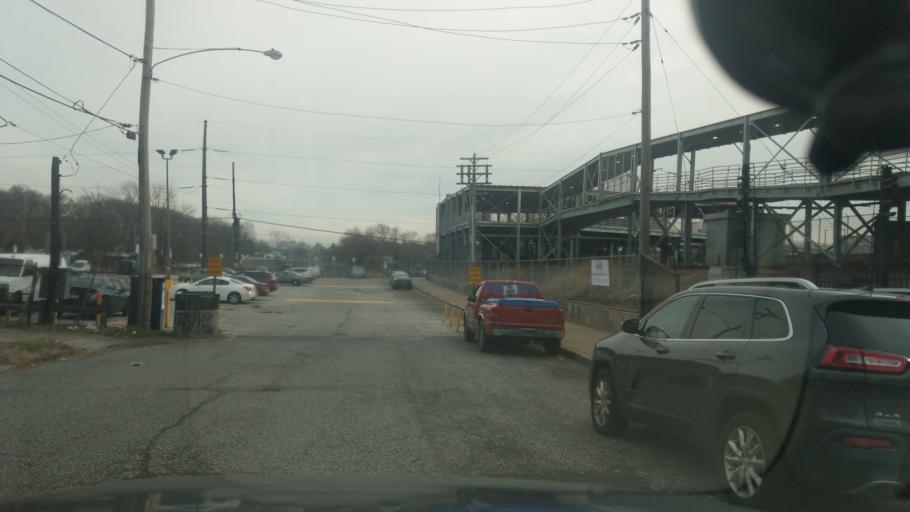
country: US
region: Pennsylvania
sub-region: Montgomery County
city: Wyncote
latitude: 40.0419
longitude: -75.1361
